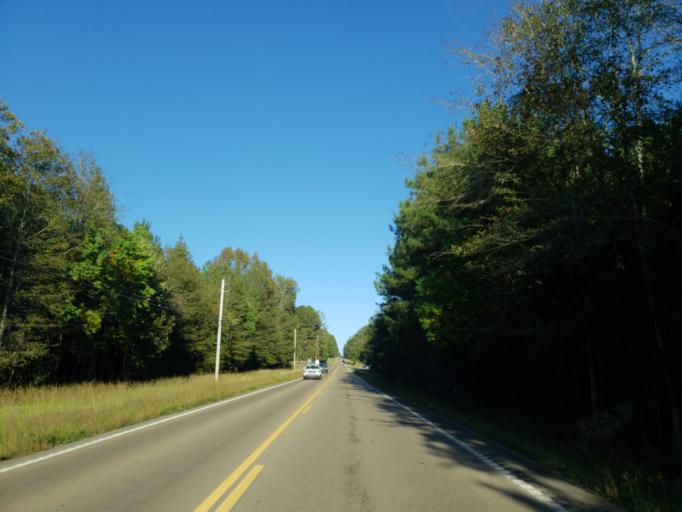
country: US
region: Mississippi
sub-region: Perry County
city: Richton
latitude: 31.3566
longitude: -88.9113
